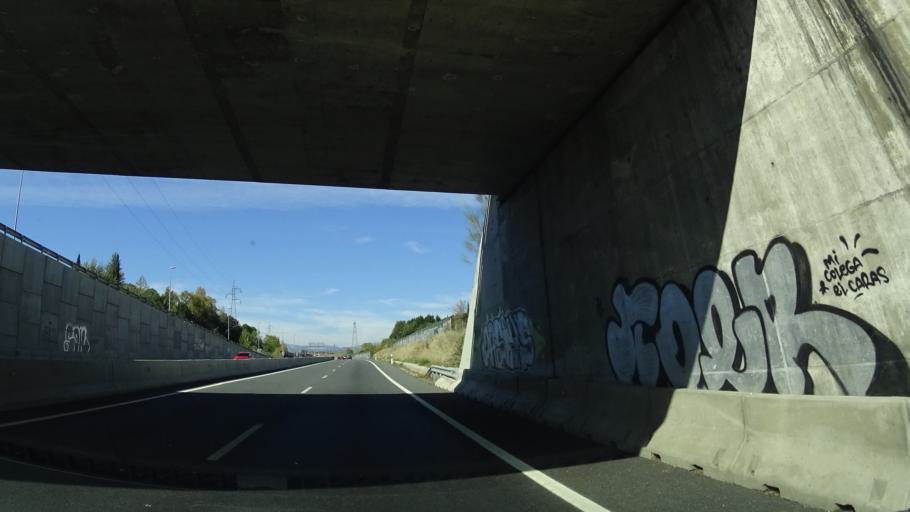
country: ES
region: Madrid
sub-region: Provincia de Madrid
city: Villanueva del Pardillo
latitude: 40.4871
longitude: -3.9456
